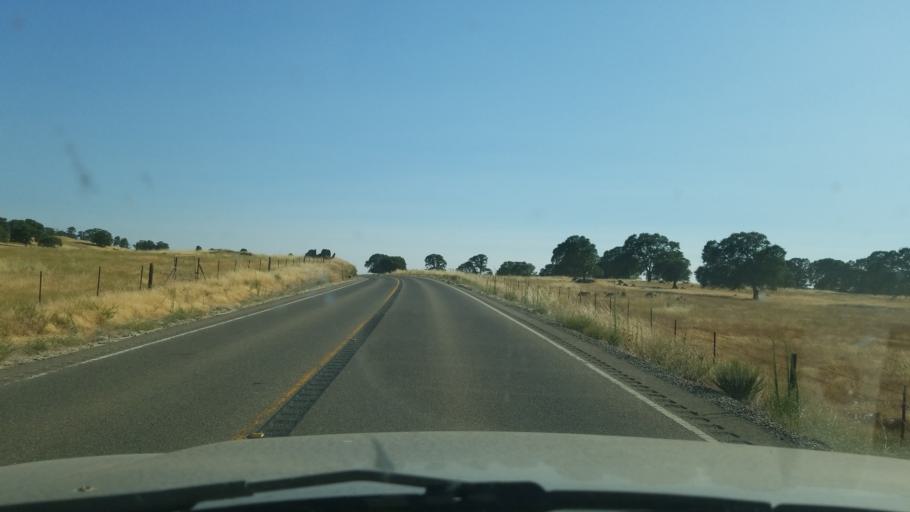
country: US
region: California
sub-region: Tuolumne County
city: Jamestown
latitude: 37.7783
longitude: -120.4682
